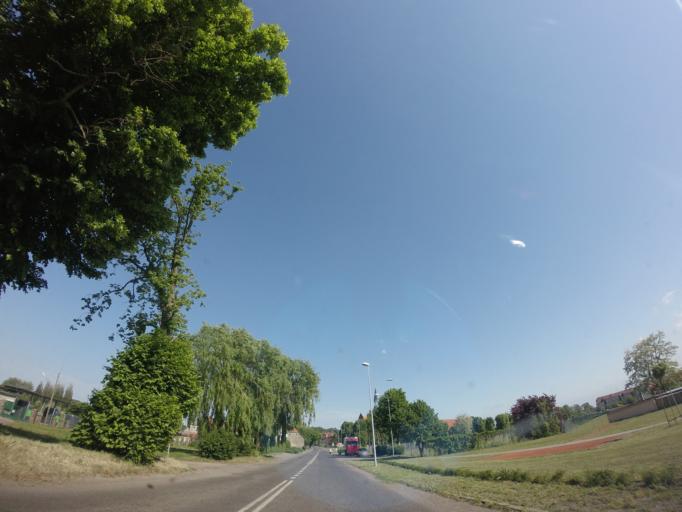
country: PL
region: West Pomeranian Voivodeship
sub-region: Powiat gryfinski
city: Stare Czarnowo
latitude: 53.3027
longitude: 14.8106
